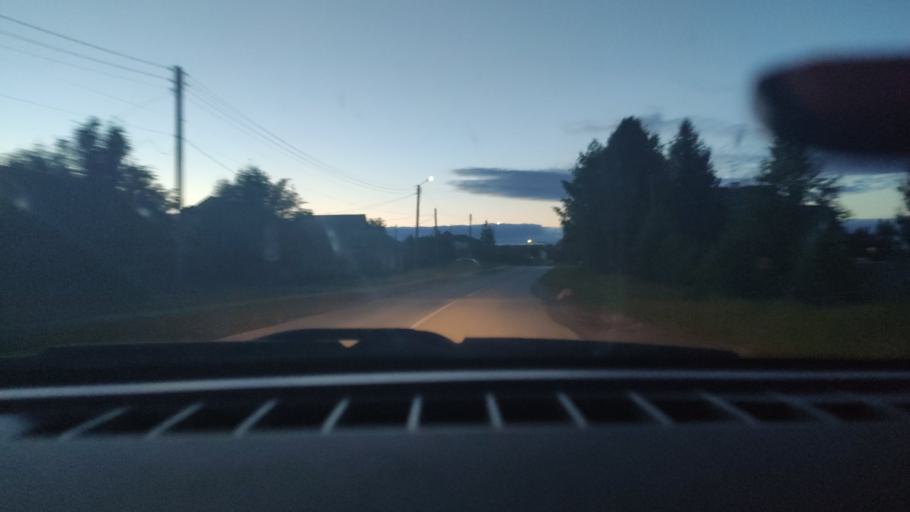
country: RU
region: Perm
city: Polazna
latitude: 58.2792
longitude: 56.4075
